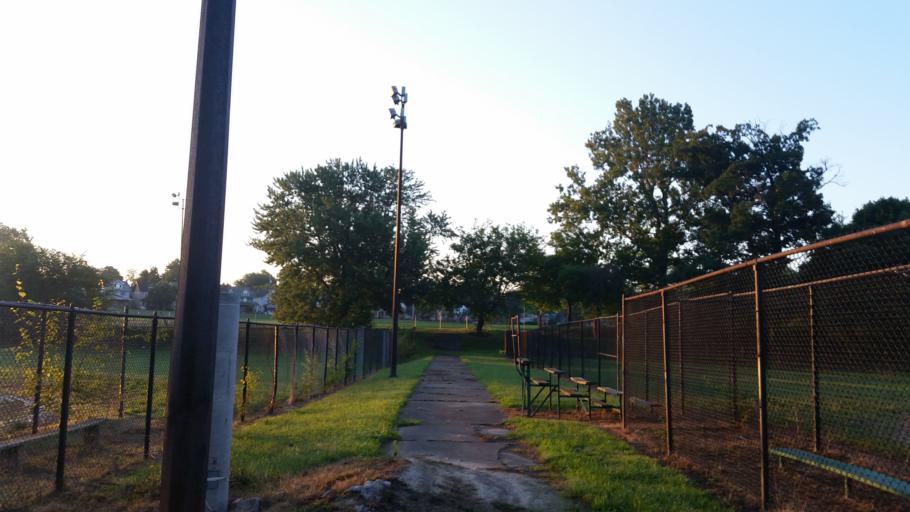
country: US
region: Ohio
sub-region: Cuyahoga County
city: Bratenahl
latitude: 41.5467
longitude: -81.6095
